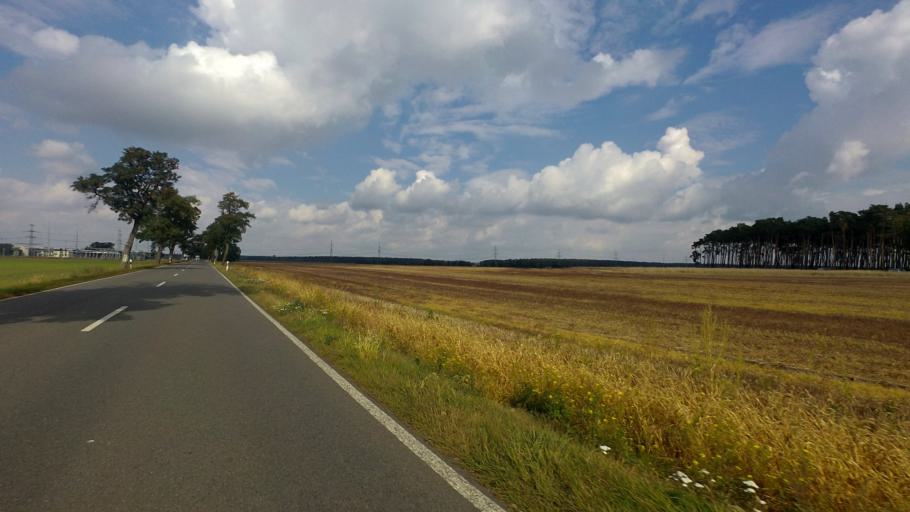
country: DE
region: Saxony-Anhalt
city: Holzdorf
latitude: 51.8221
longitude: 13.1657
